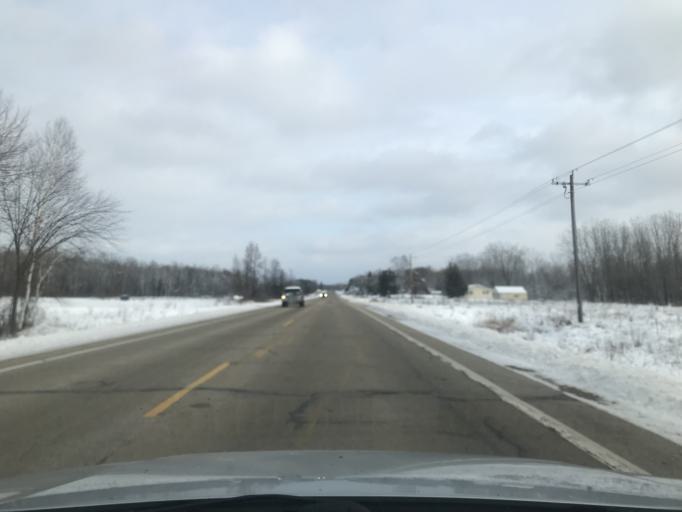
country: US
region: Wisconsin
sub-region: Oconto County
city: Oconto Falls
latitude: 44.8869
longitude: -88.0310
